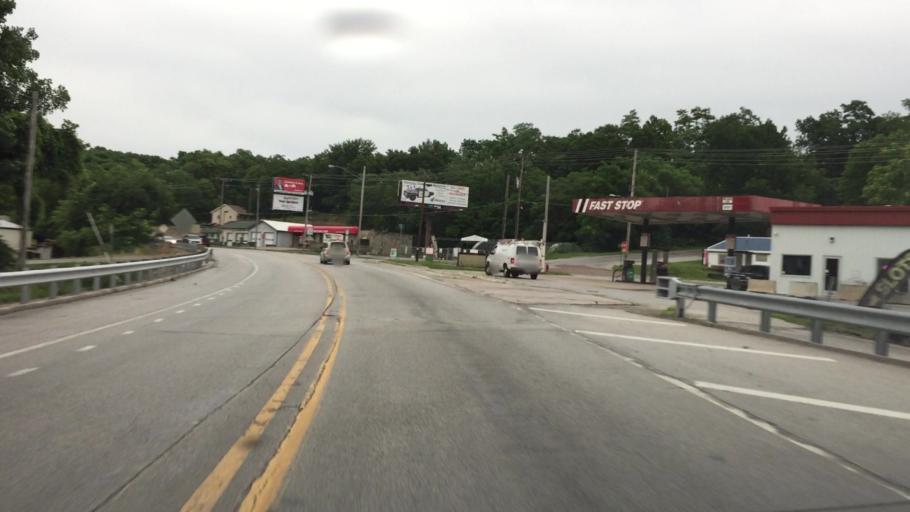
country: US
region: Illinois
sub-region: Hancock County
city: Hamilton
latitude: 40.3911
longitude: -91.3565
